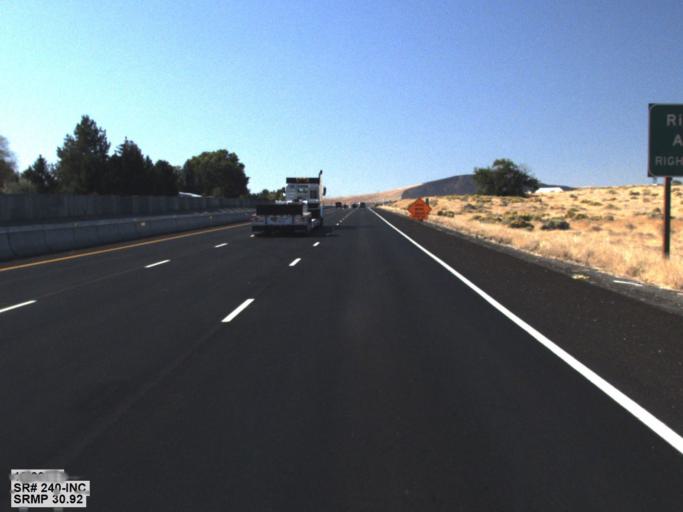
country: US
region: Washington
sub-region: Benton County
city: Richland
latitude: 46.3056
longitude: -119.2901
